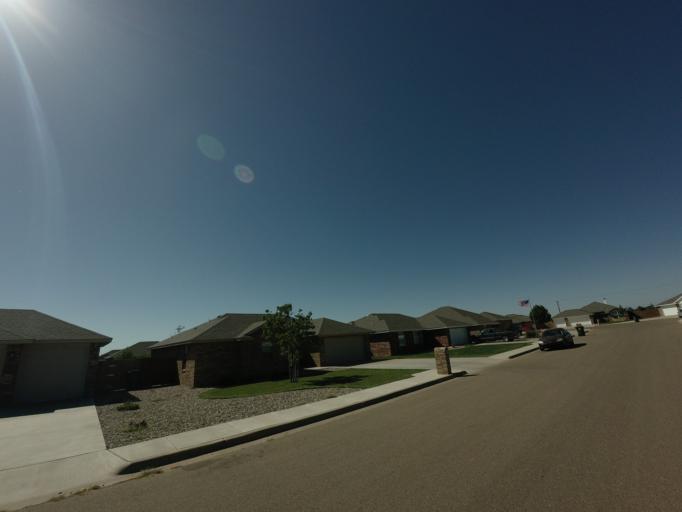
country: US
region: New Mexico
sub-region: Curry County
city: Clovis
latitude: 34.4228
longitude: -103.1592
